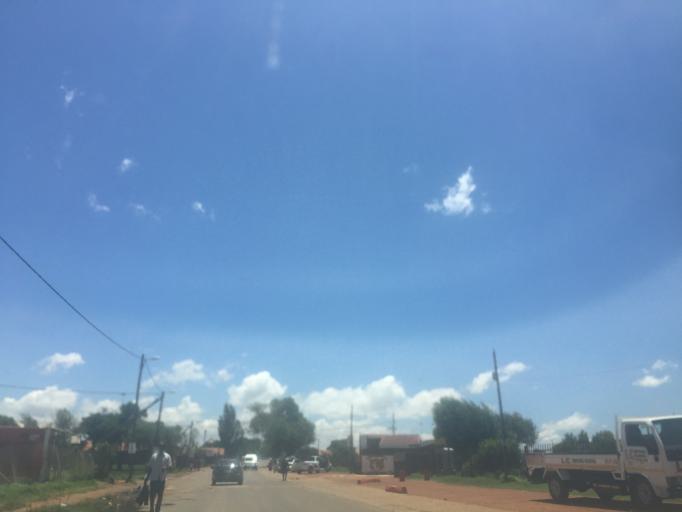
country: ZA
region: Mpumalanga
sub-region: Nkangala District Municipality
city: Delmas
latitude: -26.1314
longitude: 28.6938
